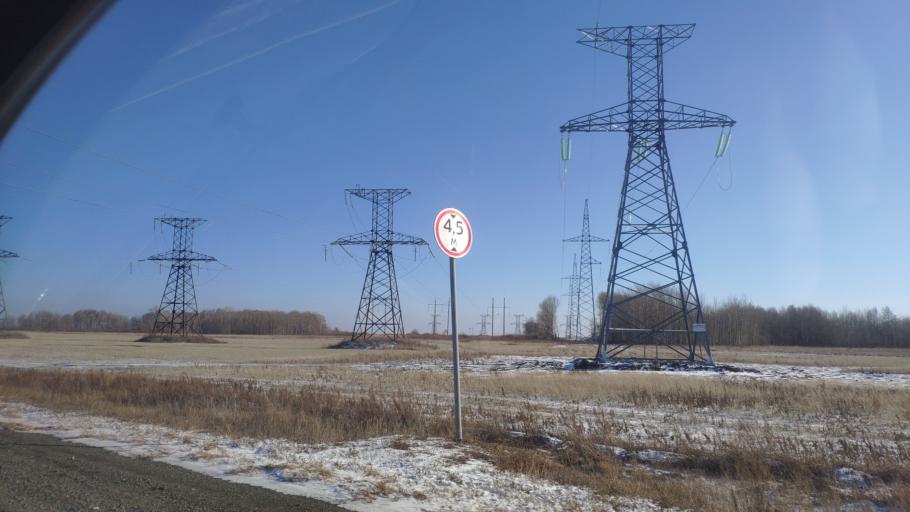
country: RU
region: Orenburg
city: Mednogorsk
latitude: 51.3223
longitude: 57.6020
